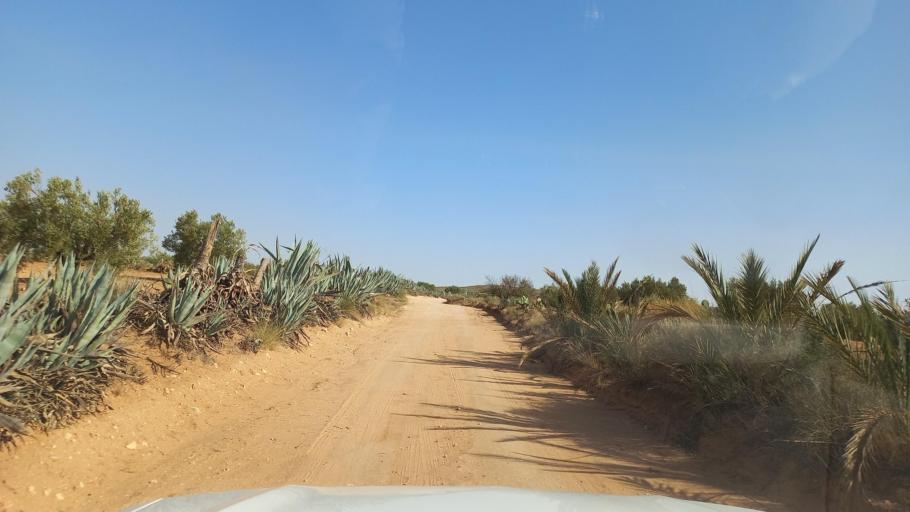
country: TN
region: Al Qasrayn
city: Kasserine
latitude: 35.2043
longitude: 8.9616
